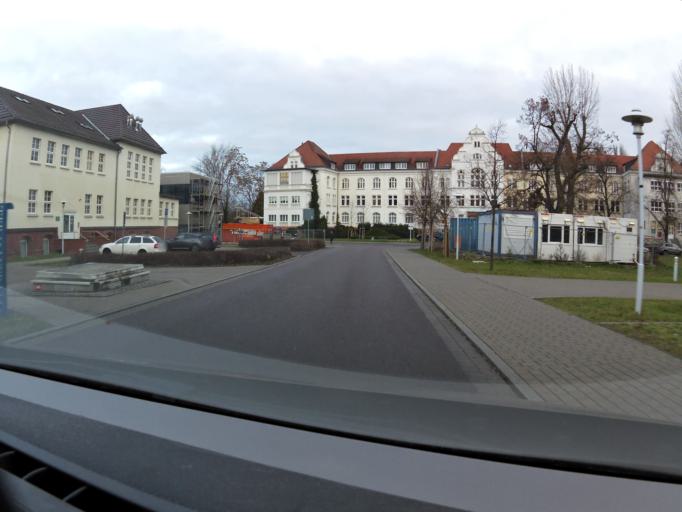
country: DE
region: Saxony-Anhalt
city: Magdeburg
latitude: 52.1027
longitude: 11.6179
